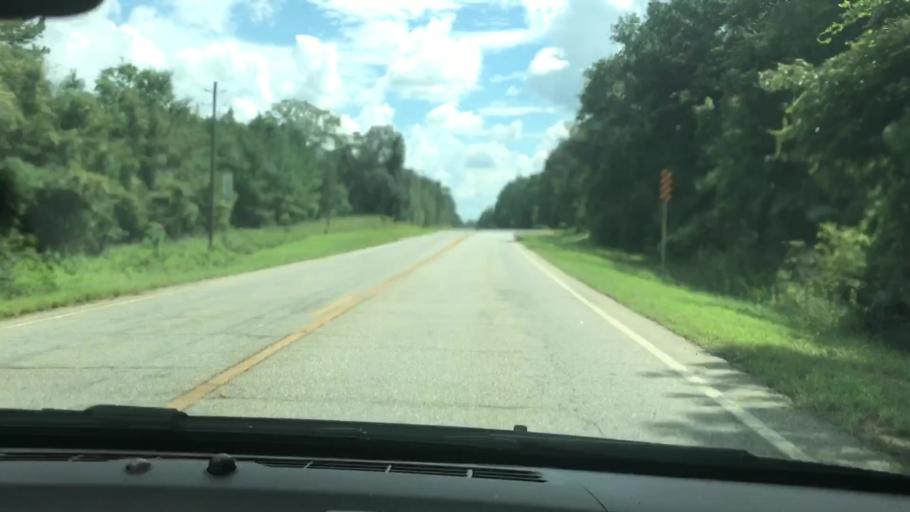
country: US
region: Georgia
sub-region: Clay County
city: Fort Gaines
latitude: 31.6640
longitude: -85.0472
